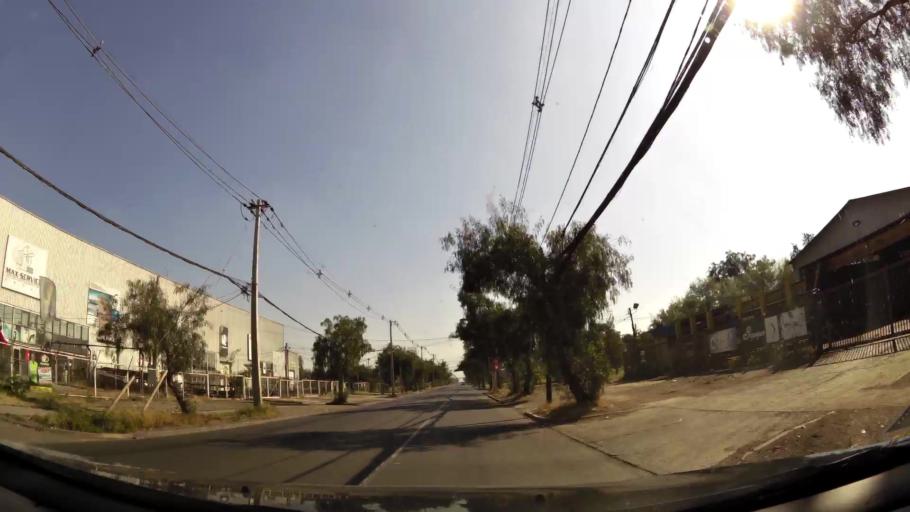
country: CL
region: Santiago Metropolitan
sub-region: Provincia de Chacabuco
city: Chicureo Abajo
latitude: -33.3358
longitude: -70.7201
